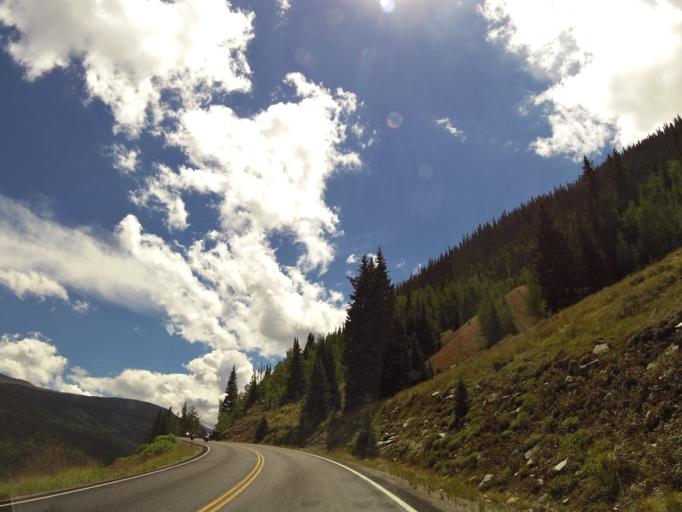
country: US
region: Colorado
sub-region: San Juan County
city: Silverton
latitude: 37.7962
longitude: -107.6743
